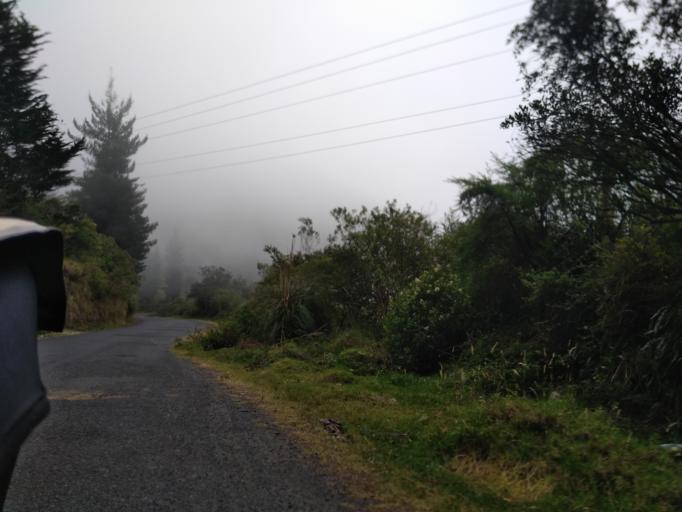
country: EC
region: Cotopaxi
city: Saquisili
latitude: -0.6867
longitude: -78.8332
